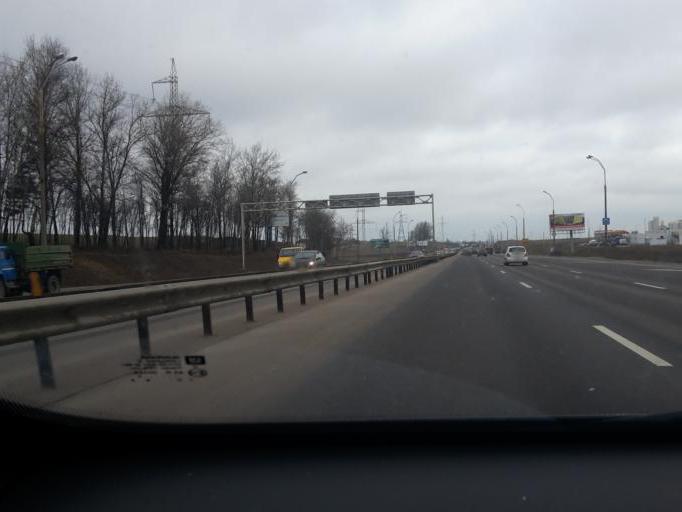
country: BY
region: Minsk
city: Zhdanovichy
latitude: 53.9136
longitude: 27.4110
